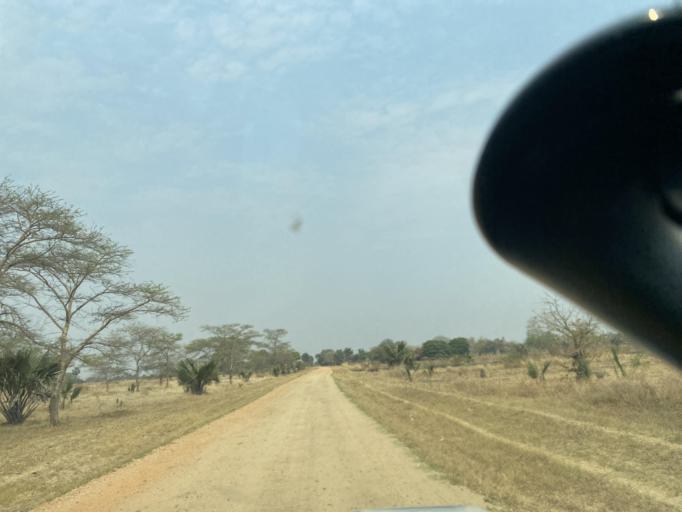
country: ZM
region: Lusaka
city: Kafue
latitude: -15.6480
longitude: 28.0370
